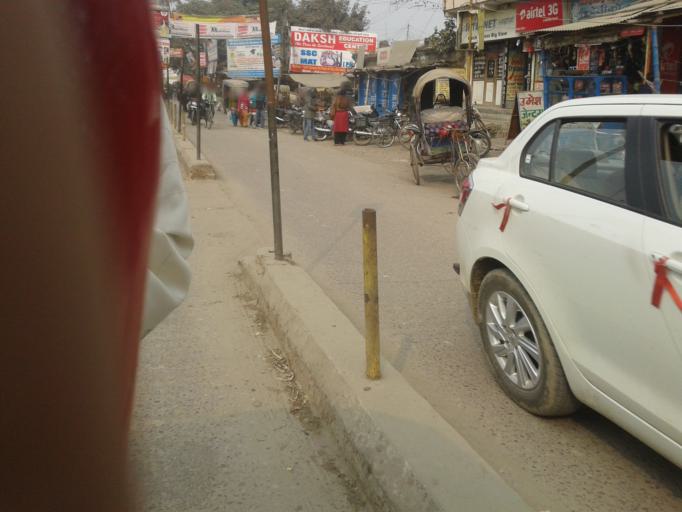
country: IN
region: Bihar
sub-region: Muzaffarpur
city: Muzaffarpur
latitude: 26.1133
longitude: 85.3965
